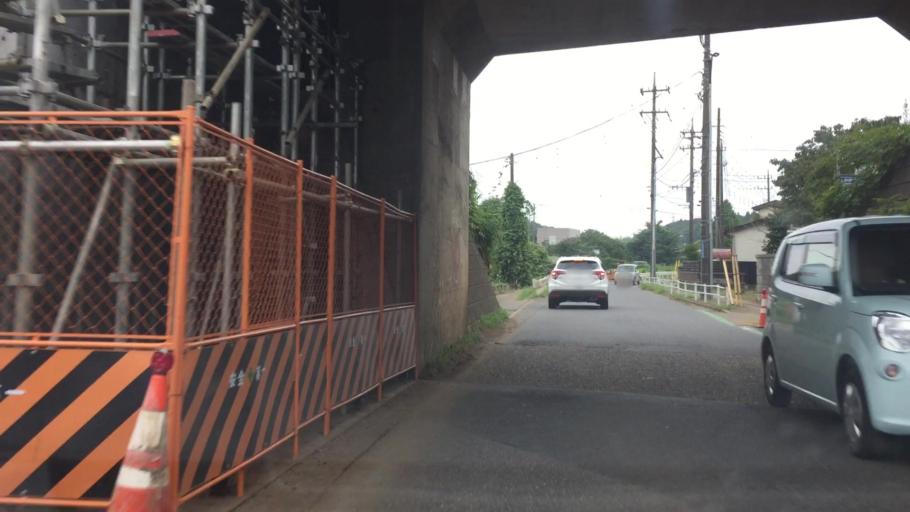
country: JP
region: Chiba
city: Kashiwa
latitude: 35.8192
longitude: 139.9885
